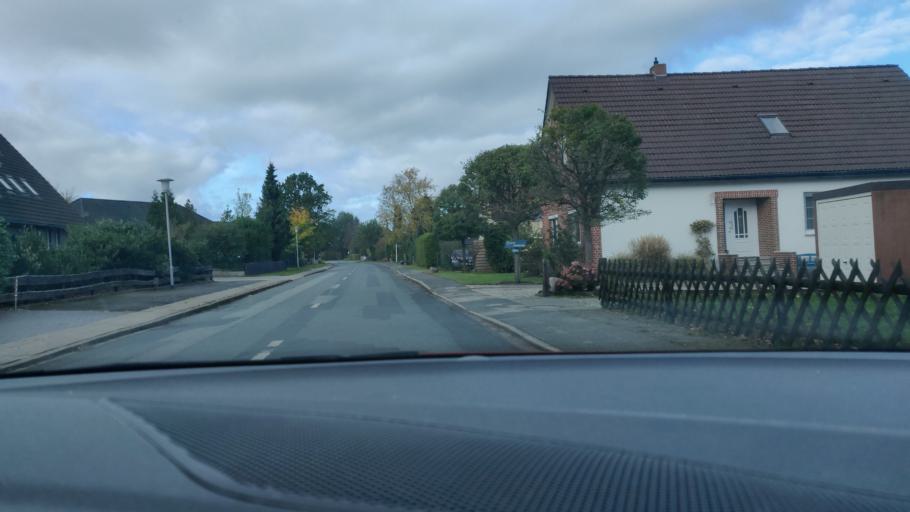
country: DE
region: Lower Saxony
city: Cuxhaven
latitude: 53.8302
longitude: 8.6695
